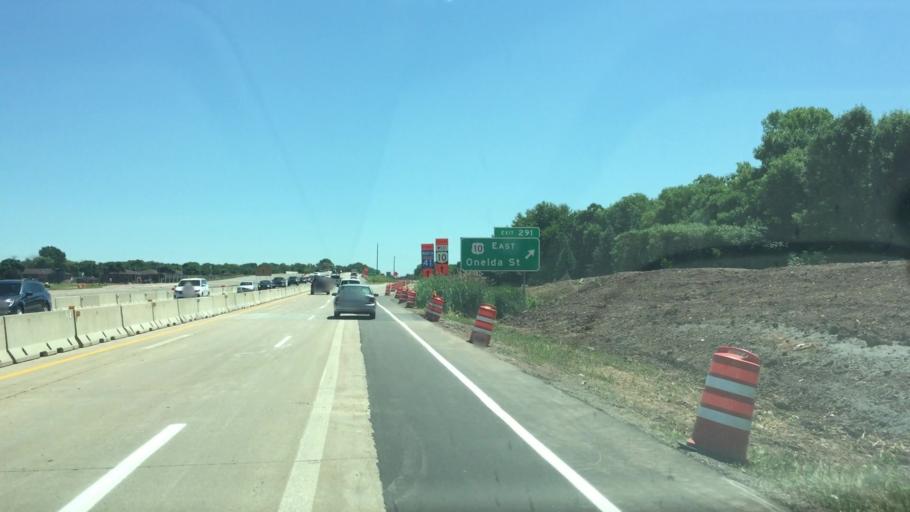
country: US
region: Wisconsin
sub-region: Outagamie County
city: Appleton
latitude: 44.2336
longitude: -88.4104
